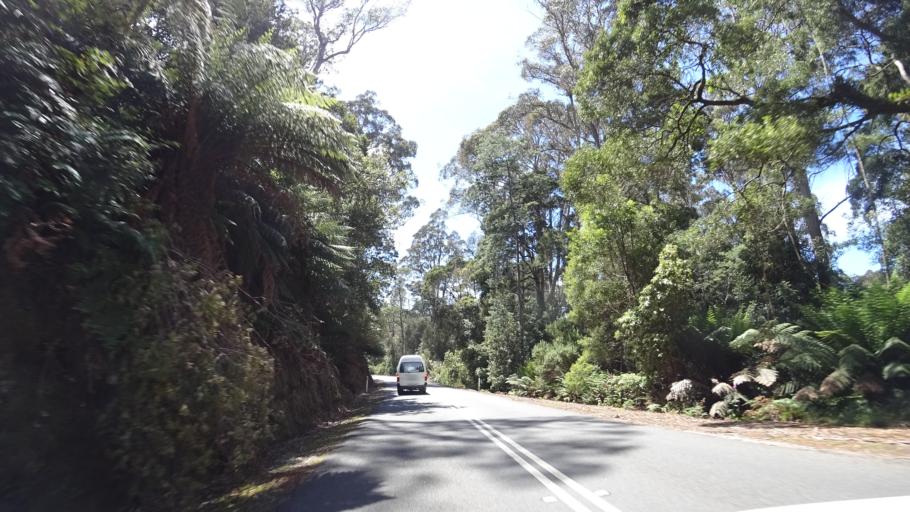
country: AU
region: Tasmania
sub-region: Break O'Day
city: St Helens
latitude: -41.1586
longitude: 147.8971
